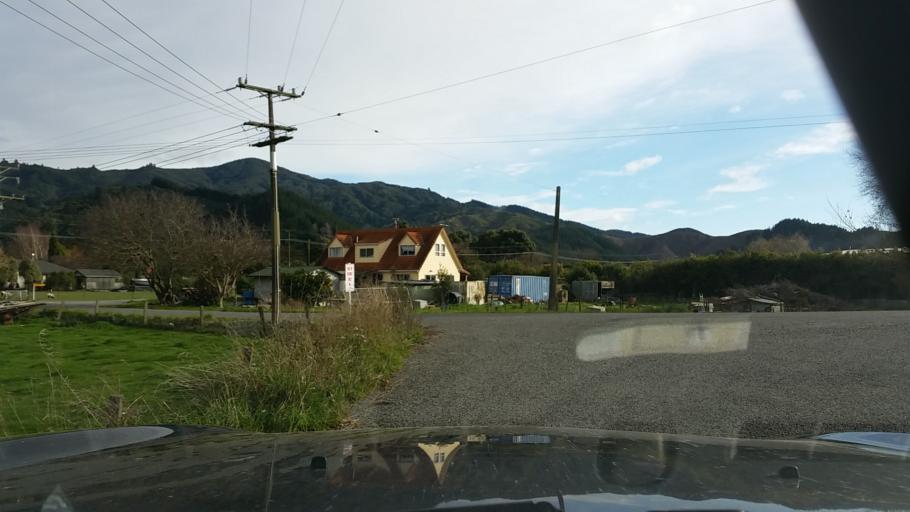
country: NZ
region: Marlborough
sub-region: Marlborough District
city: Blenheim
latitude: -41.4276
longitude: 173.9583
